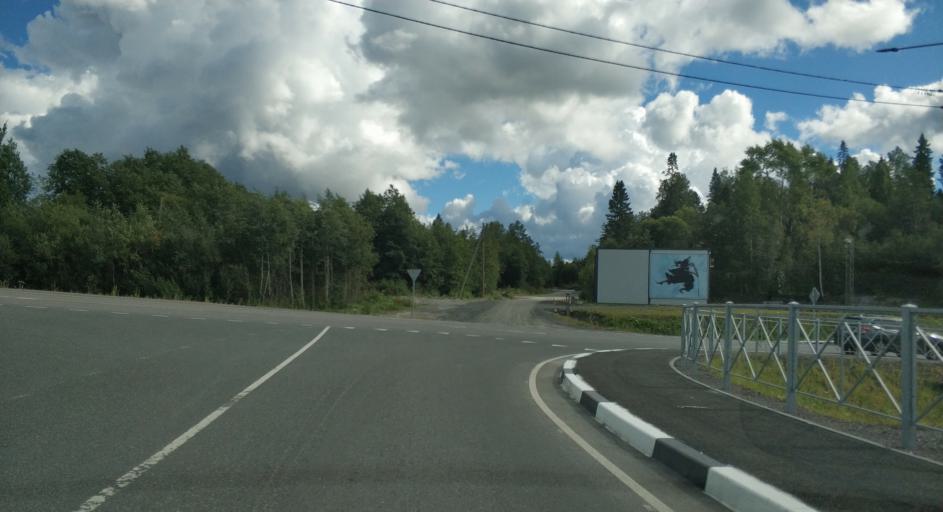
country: RU
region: Republic of Karelia
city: Ruskeala
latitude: 61.9464
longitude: 30.5981
